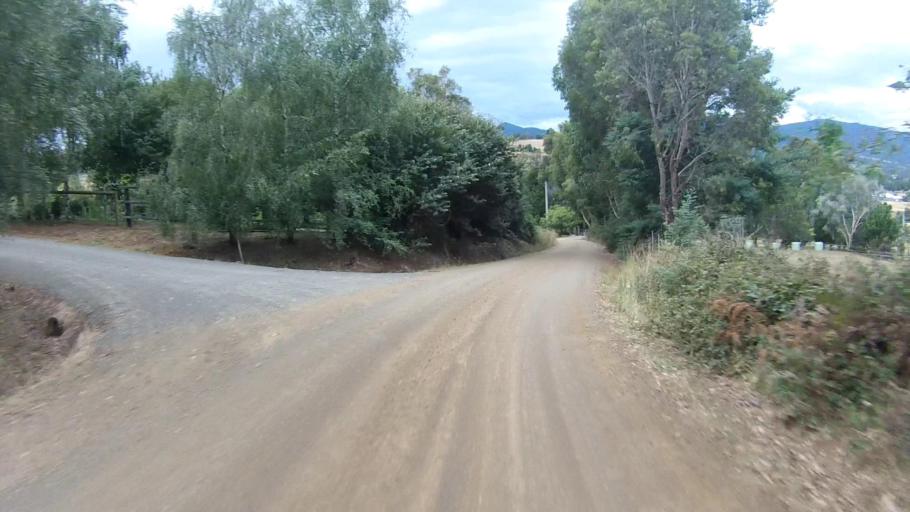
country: AU
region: Tasmania
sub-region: Huon Valley
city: Huonville
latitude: -42.9702
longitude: 147.0504
